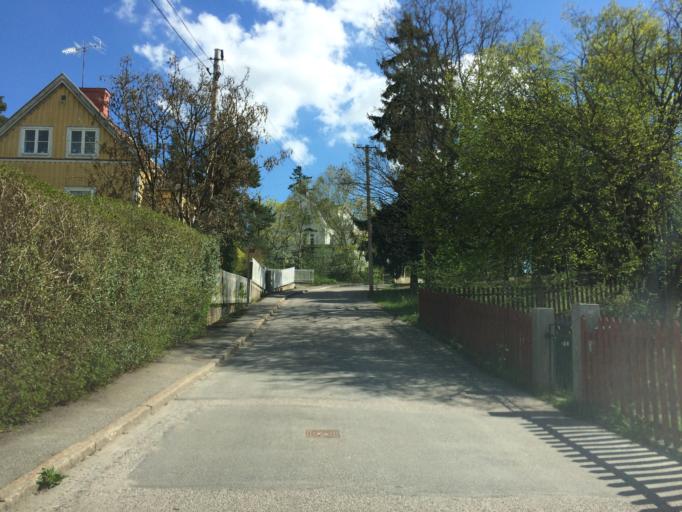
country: SE
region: Stockholm
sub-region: Huddinge Kommun
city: Segeltorp
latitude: 59.3034
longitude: 17.9623
